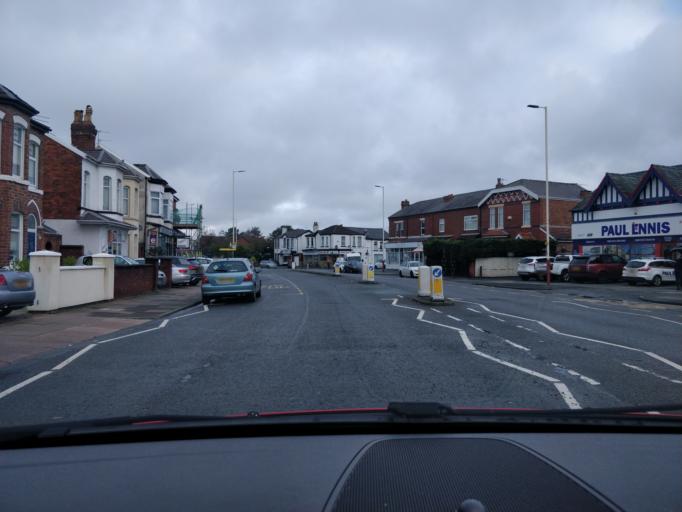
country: GB
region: England
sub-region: Sefton
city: Southport
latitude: 53.6220
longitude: -3.0126
